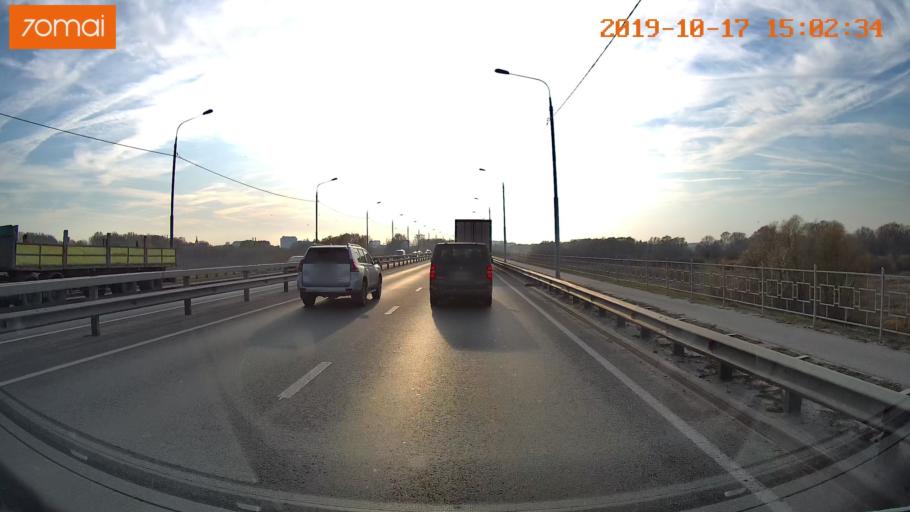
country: RU
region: Rjazan
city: Ryazan'
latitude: 54.6453
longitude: 39.7407
